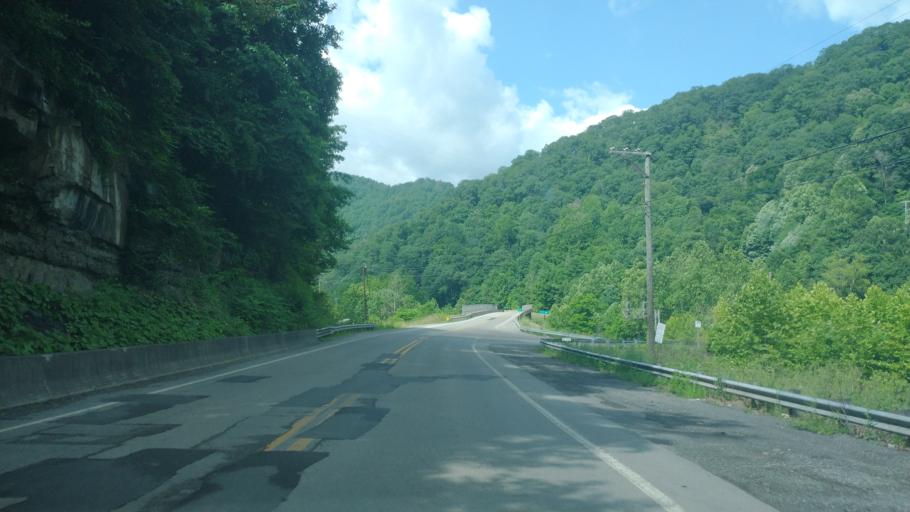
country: US
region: West Virginia
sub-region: McDowell County
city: Welch
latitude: 37.4092
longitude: -81.4595
